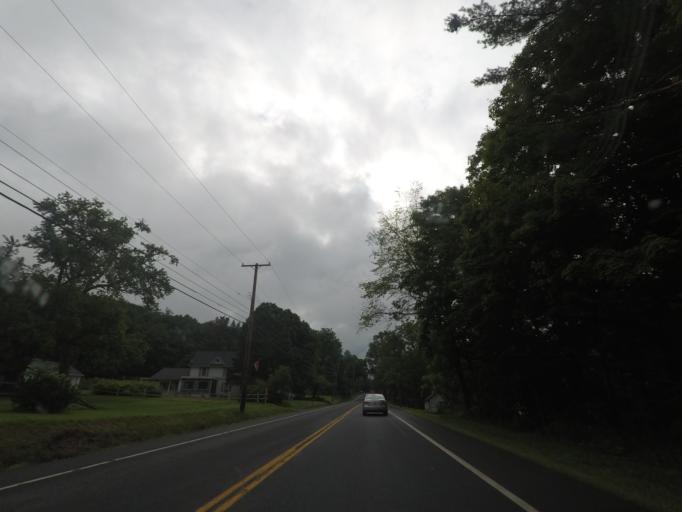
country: US
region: New York
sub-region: Rensselaer County
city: Nassau
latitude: 42.4954
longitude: -73.5158
